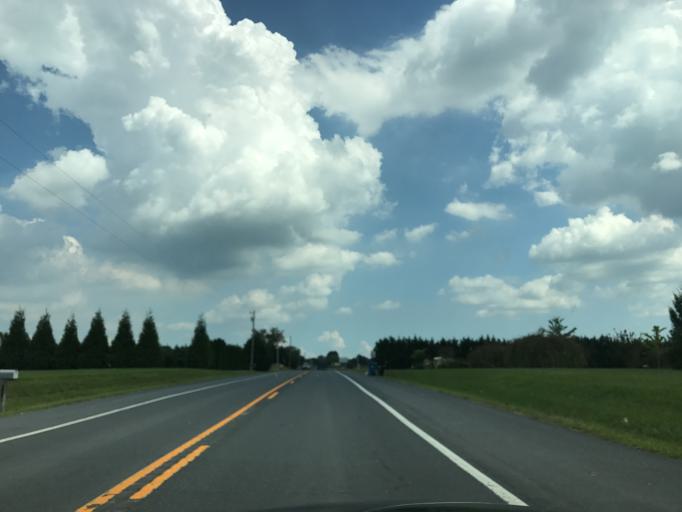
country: US
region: Delaware
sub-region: Kent County
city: Clayton
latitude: 39.1995
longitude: -75.7525
